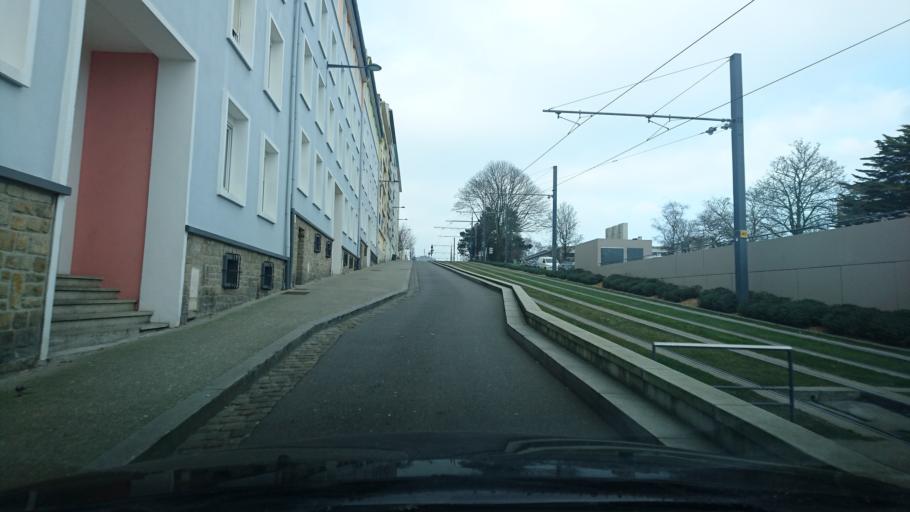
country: FR
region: Brittany
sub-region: Departement du Finistere
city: Brest
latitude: 48.3849
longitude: -4.5040
